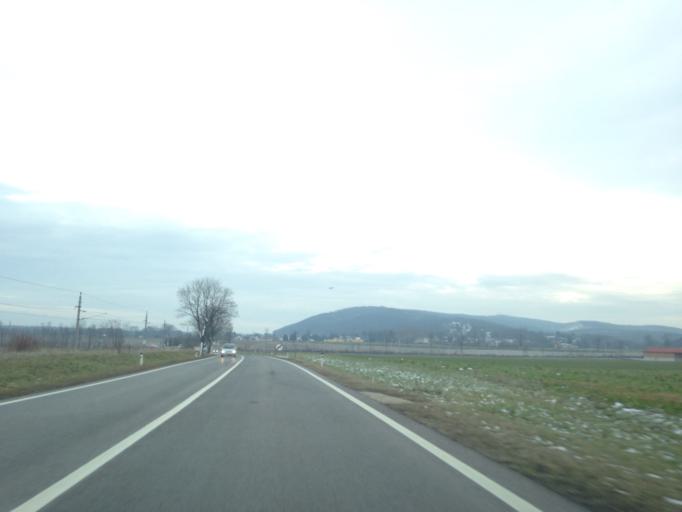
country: AT
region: Lower Austria
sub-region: Politischer Bezirk Bruck an der Leitha
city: Wolfsthal
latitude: 48.1411
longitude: 16.9890
